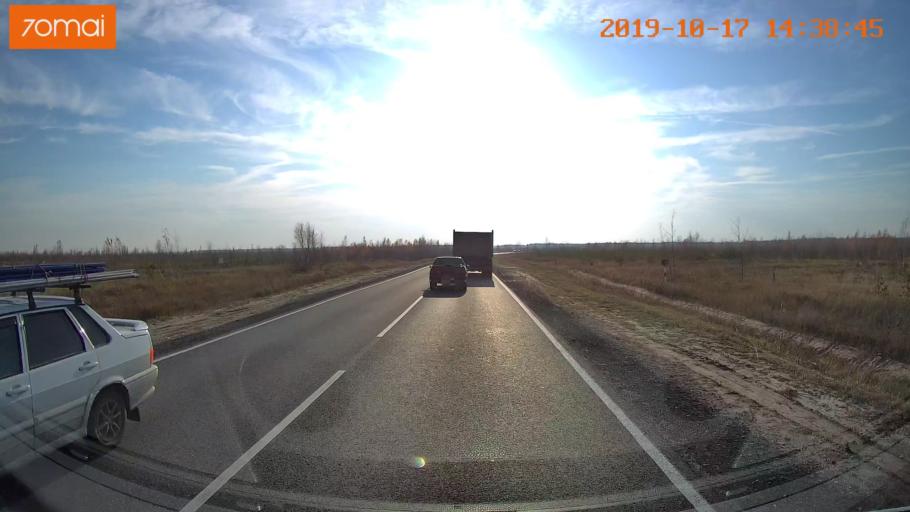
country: RU
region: Rjazan
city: Solotcha
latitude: 54.8678
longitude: 39.9823
